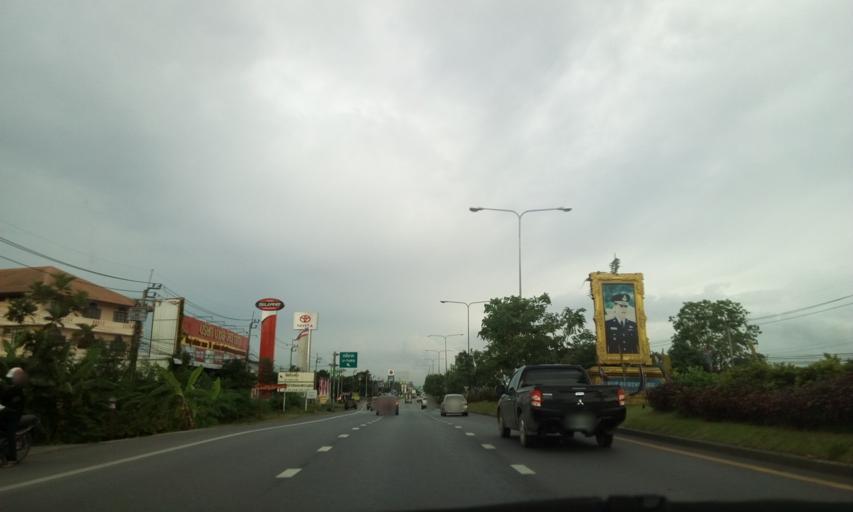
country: TH
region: Nonthaburi
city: Pak Kret
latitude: 13.9244
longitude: 100.4707
